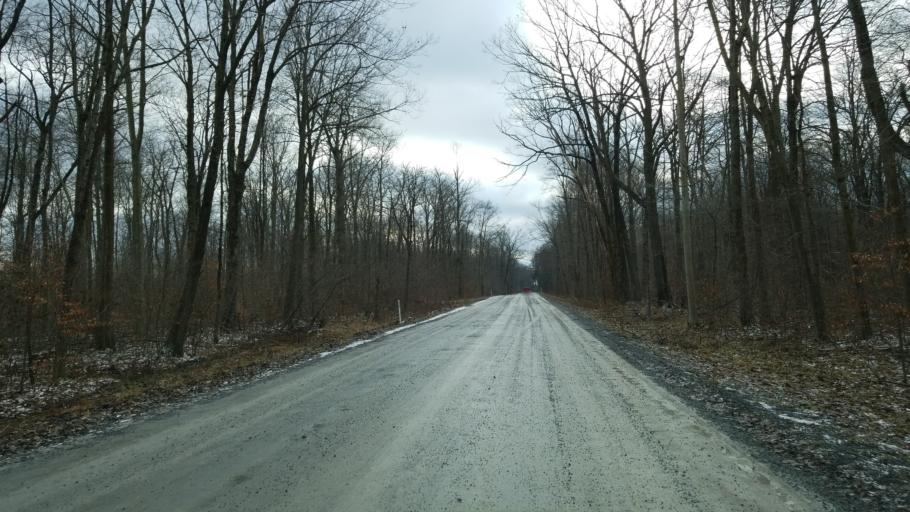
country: US
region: Pennsylvania
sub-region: Clearfield County
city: Clearfield
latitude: 41.1377
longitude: -78.5196
